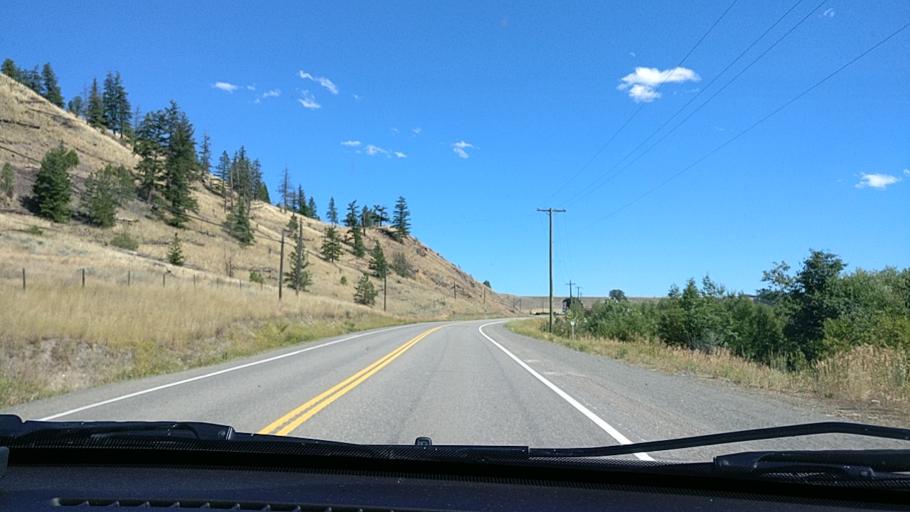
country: CA
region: British Columbia
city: Kamloops
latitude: 50.6654
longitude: -120.5598
